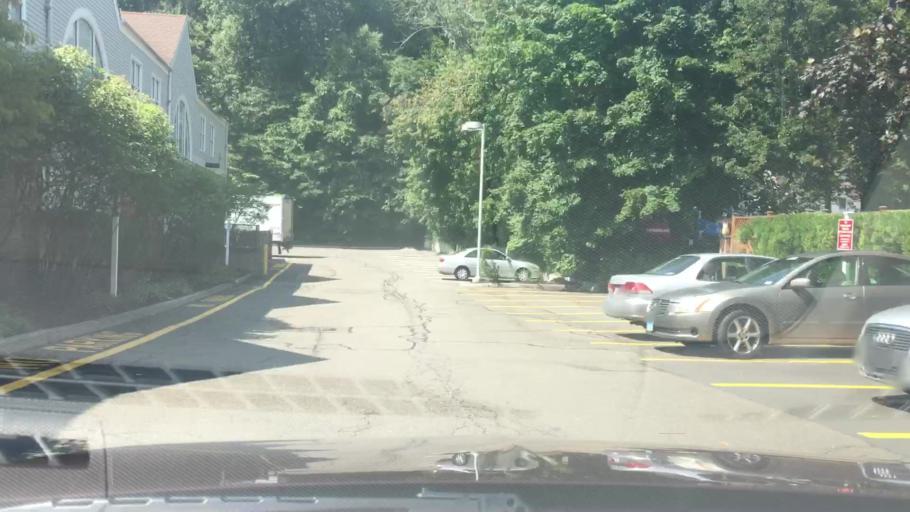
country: US
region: Connecticut
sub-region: Fairfield County
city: Wilton
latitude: 41.1915
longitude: -73.4321
